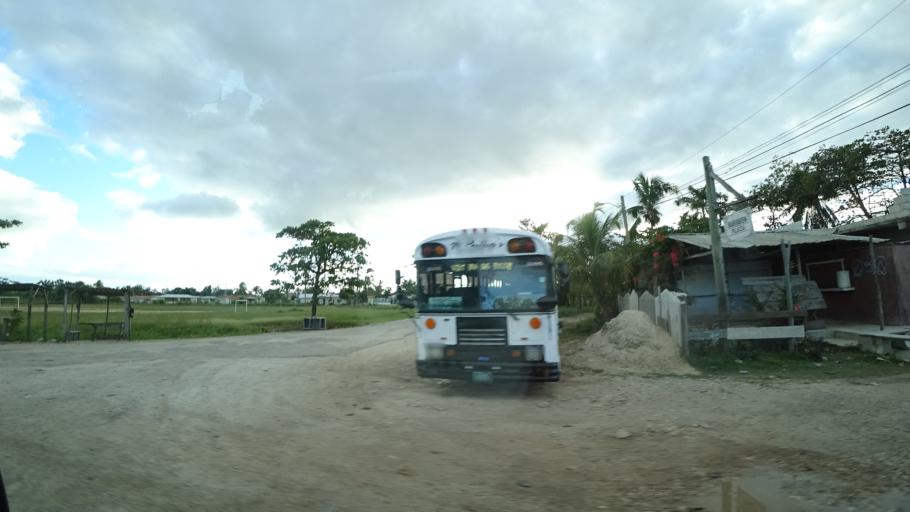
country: BZ
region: Belize
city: Belize City
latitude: 17.5515
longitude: -88.3055
